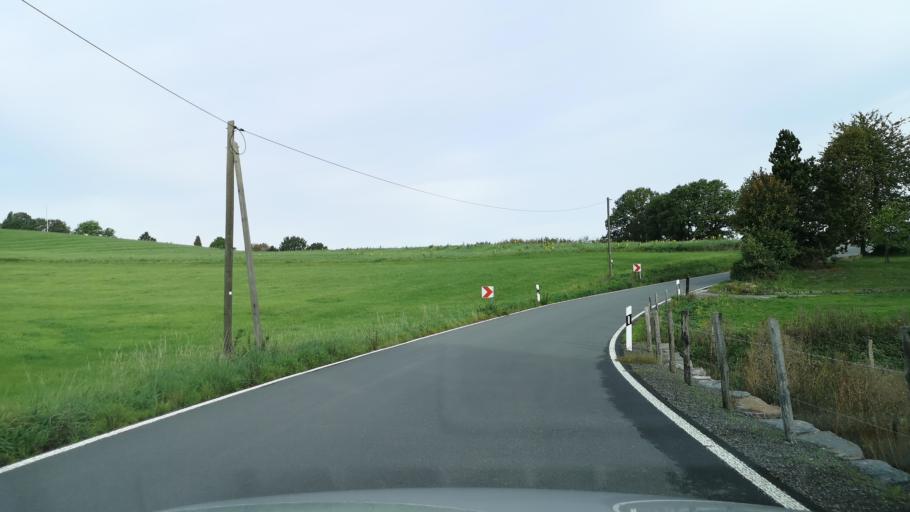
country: DE
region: North Rhine-Westphalia
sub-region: Regierungsbezirk Dusseldorf
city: Wuppertal
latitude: 51.3280
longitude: 7.1822
